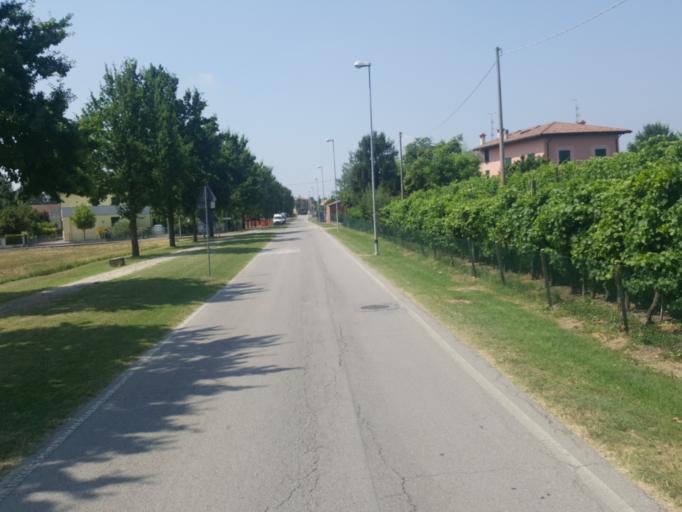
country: IT
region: Emilia-Romagna
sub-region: Provincia di Bologna
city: Castel Guelfo di Bologna
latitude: 44.4371
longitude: 11.6797
